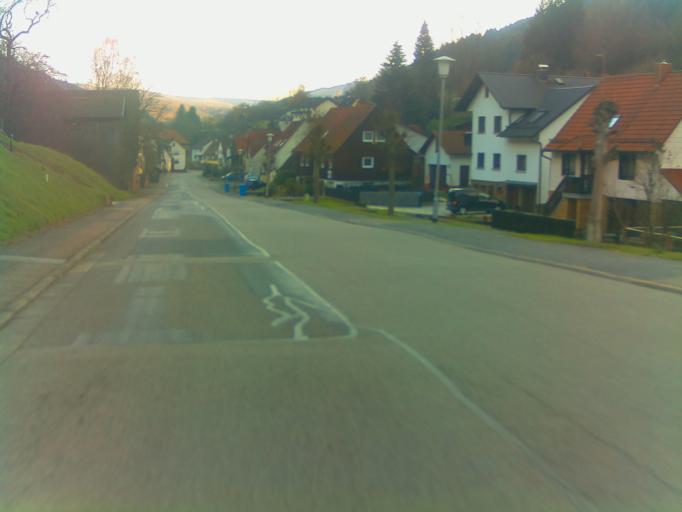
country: DE
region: Hesse
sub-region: Regierungsbezirk Darmstadt
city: Hesseneck
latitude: 49.5693
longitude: 9.0652
